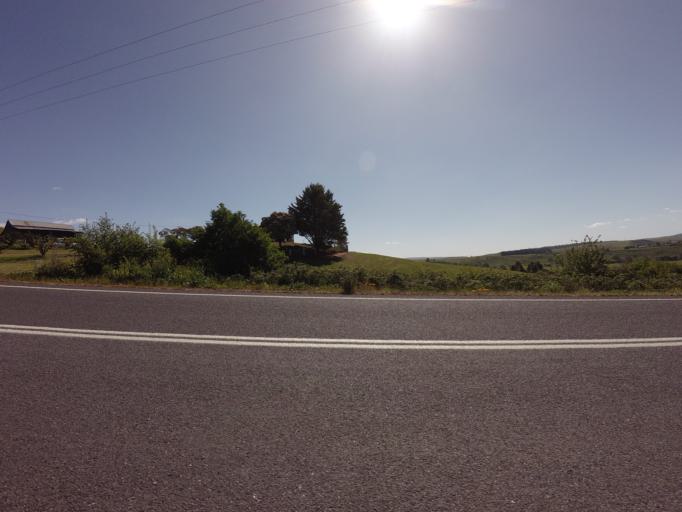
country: AU
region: Tasmania
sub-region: Derwent Valley
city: New Norfolk
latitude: -42.6947
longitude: 146.9389
